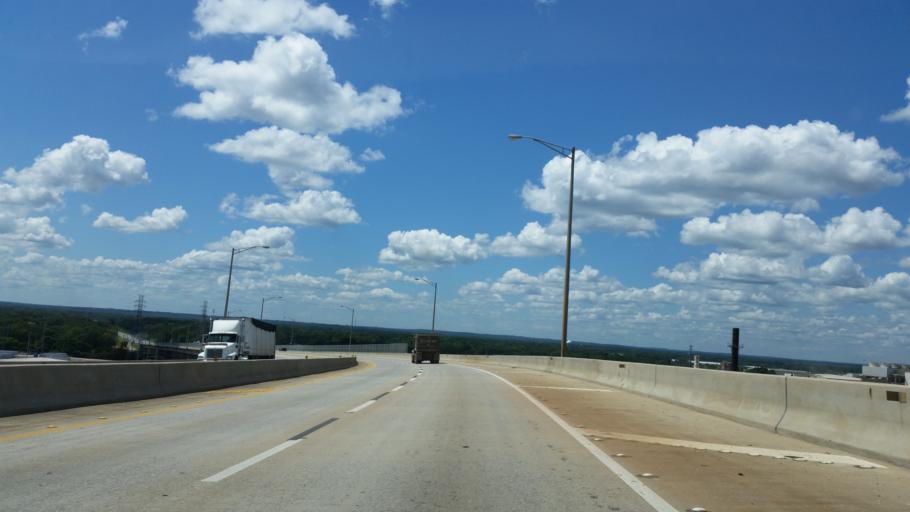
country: US
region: Alabama
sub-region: Mobile County
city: Prichard
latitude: 30.7342
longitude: -88.0450
